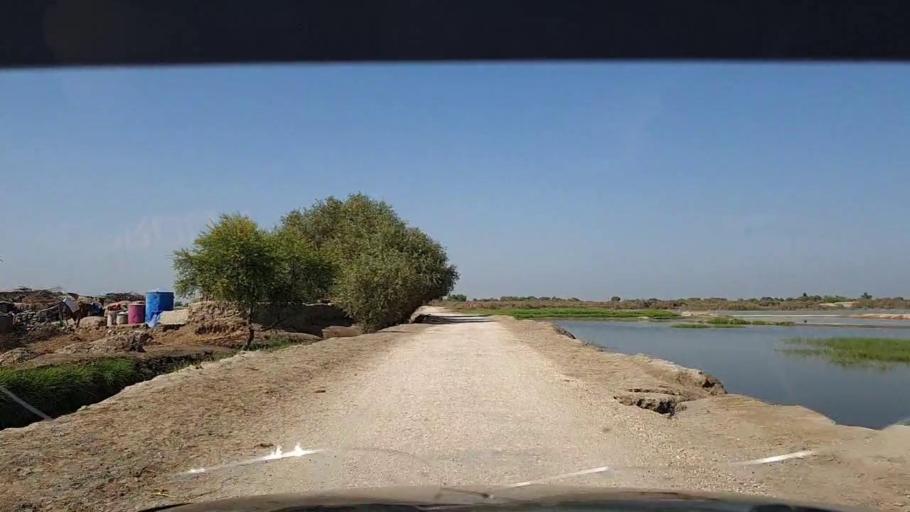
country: PK
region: Sindh
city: Tangwani
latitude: 28.3342
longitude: 69.0726
